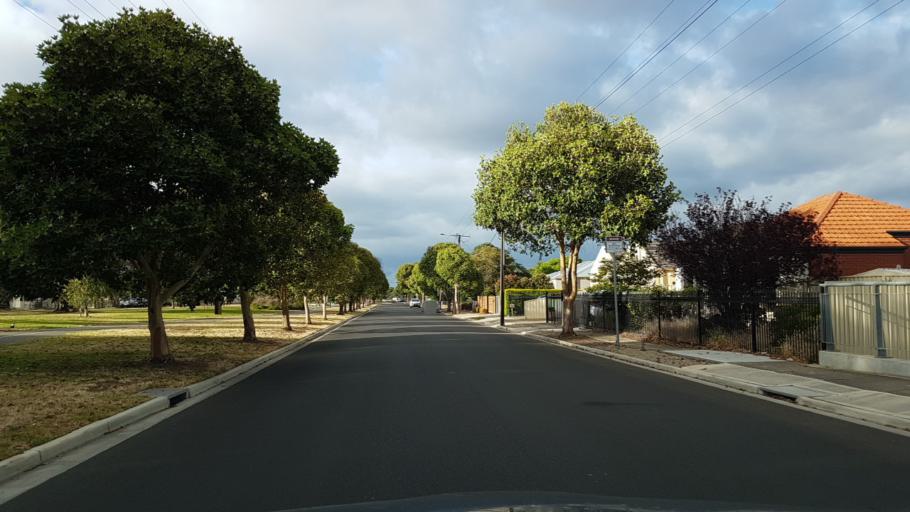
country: AU
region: South Australia
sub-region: City of West Torrens
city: Plympton
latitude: -34.9525
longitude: 138.5602
